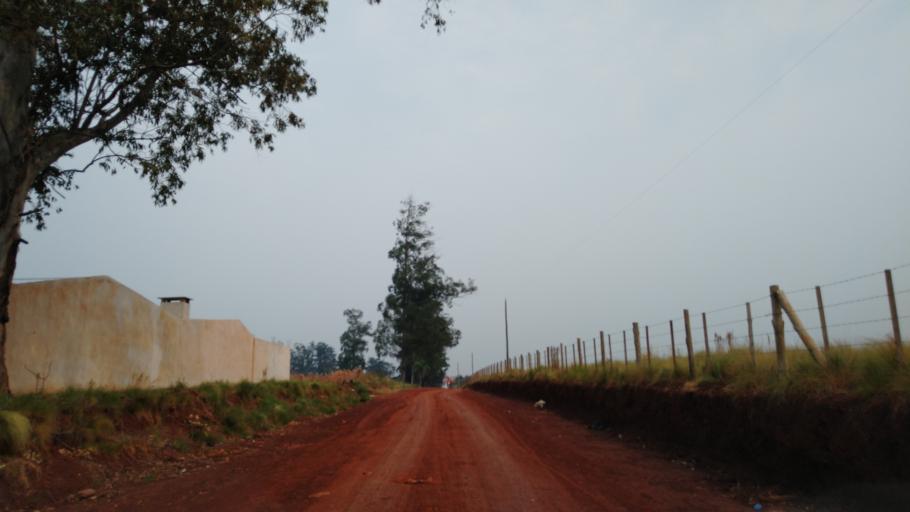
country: AR
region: Misiones
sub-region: Departamento de Capital
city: Posadas
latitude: -27.4477
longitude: -55.9346
